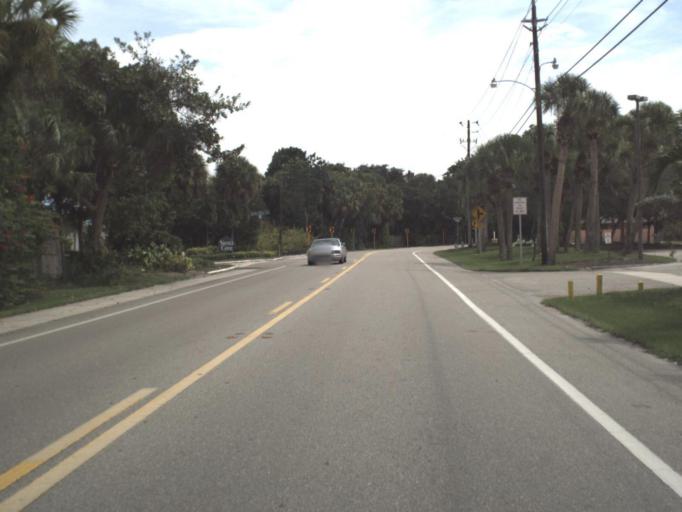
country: US
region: Florida
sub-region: Sarasota County
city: South Sarasota
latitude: 27.2743
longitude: -82.5471
